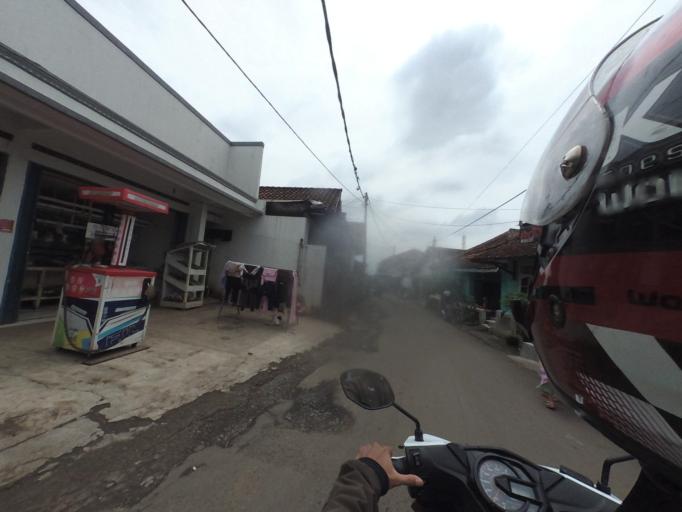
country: ID
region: West Java
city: Bogor
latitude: -6.6098
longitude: 106.7557
